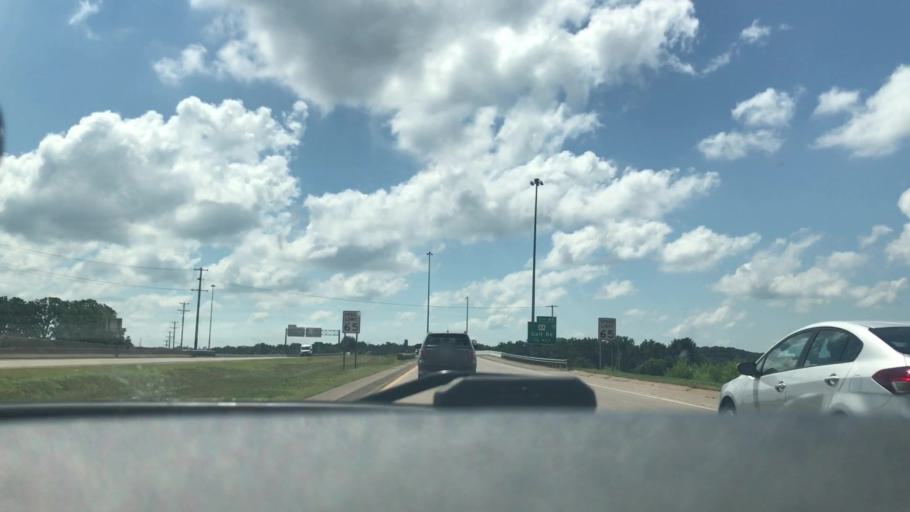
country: US
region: Wisconsin
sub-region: Eau Claire County
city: Altoona
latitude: 44.7890
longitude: -91.4535
